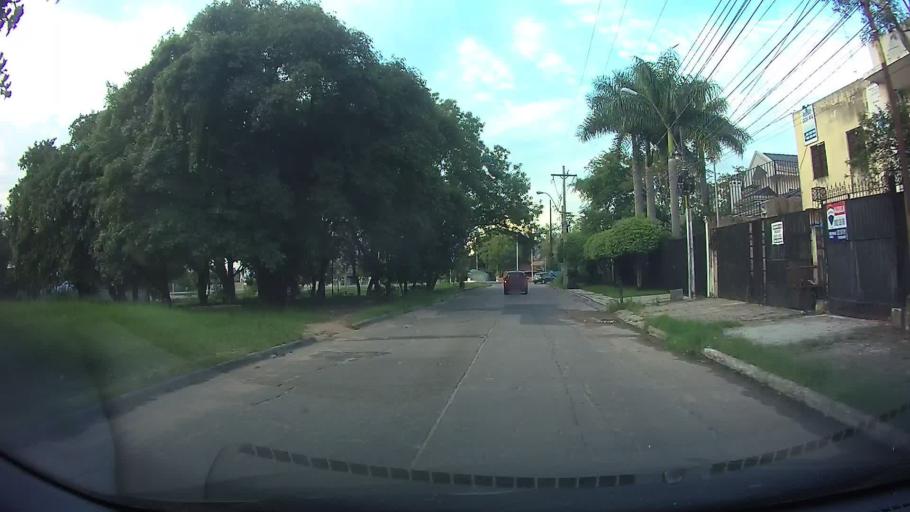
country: PY
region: Central
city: Fernando de la Mora
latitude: -25.2574
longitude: -57.5579
